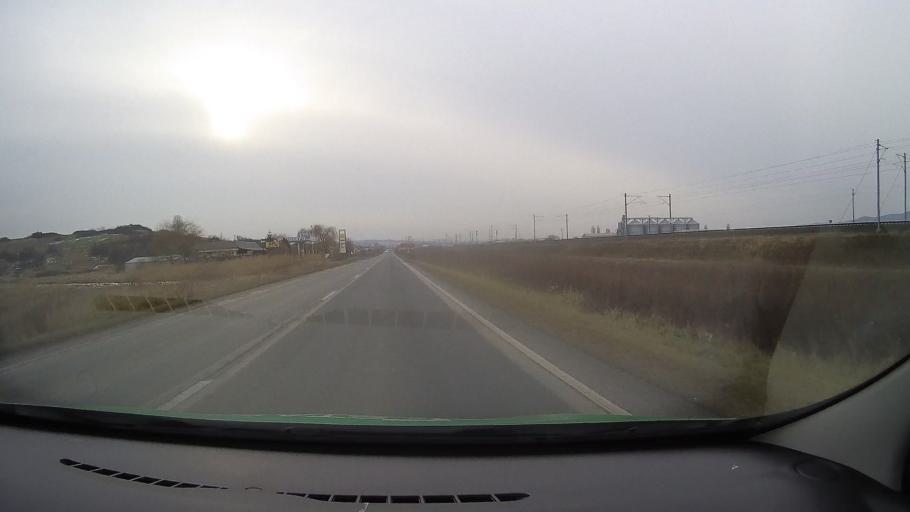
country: RO
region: Hunedoara
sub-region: Municipiul Orastie
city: Orastie
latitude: 45.8699
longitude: 23.2287
